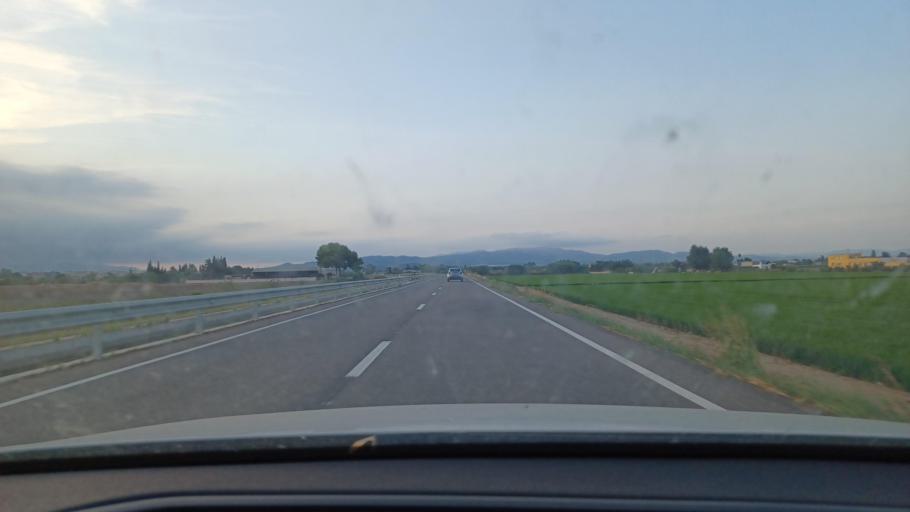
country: ES
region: Catalonia
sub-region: Provincia de Tarragona
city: Amposta
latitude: 40.6890
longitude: 0.5904
